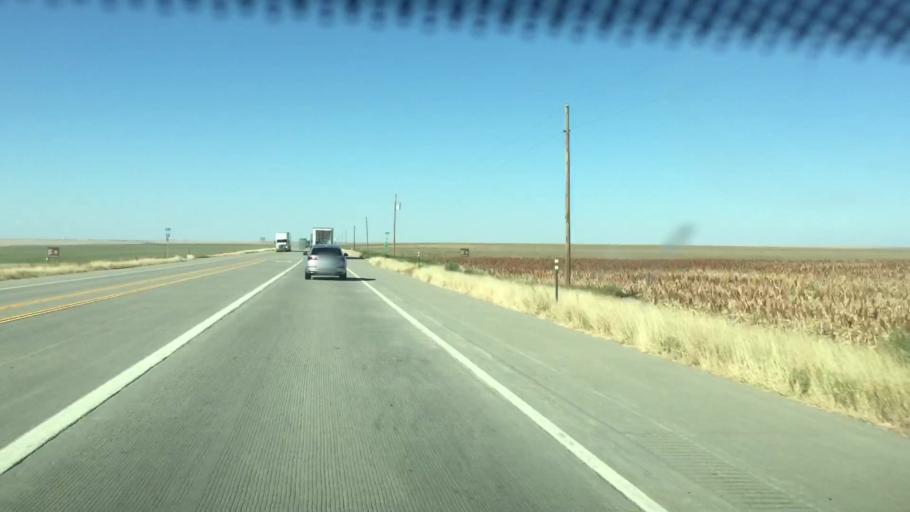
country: US
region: Colorado
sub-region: Kiowa County
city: Eads
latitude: 38.2950
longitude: -102.7199
